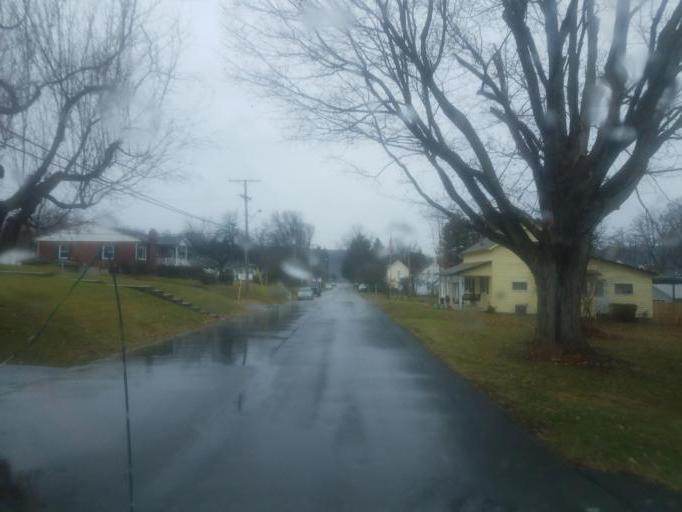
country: US
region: Ohio
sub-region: Sandusky County
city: Bellville
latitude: 40.6179
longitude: -82.5150
